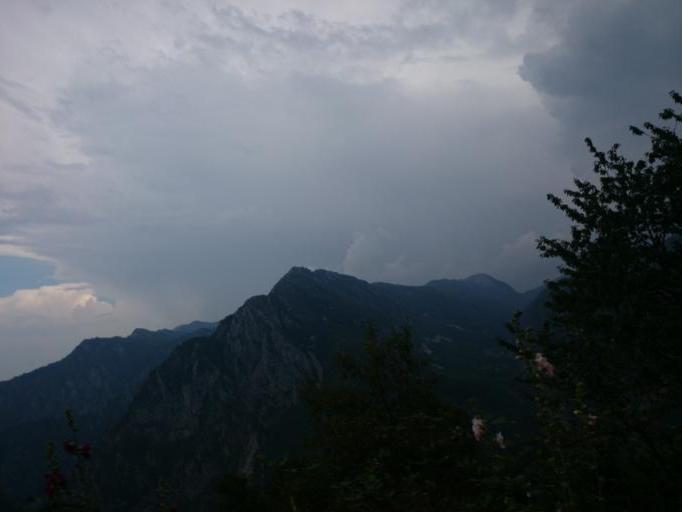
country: AL
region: Diber
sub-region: Rrethi i Dibres
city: Fushe-Lure
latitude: 41.7667
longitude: 20.2273
